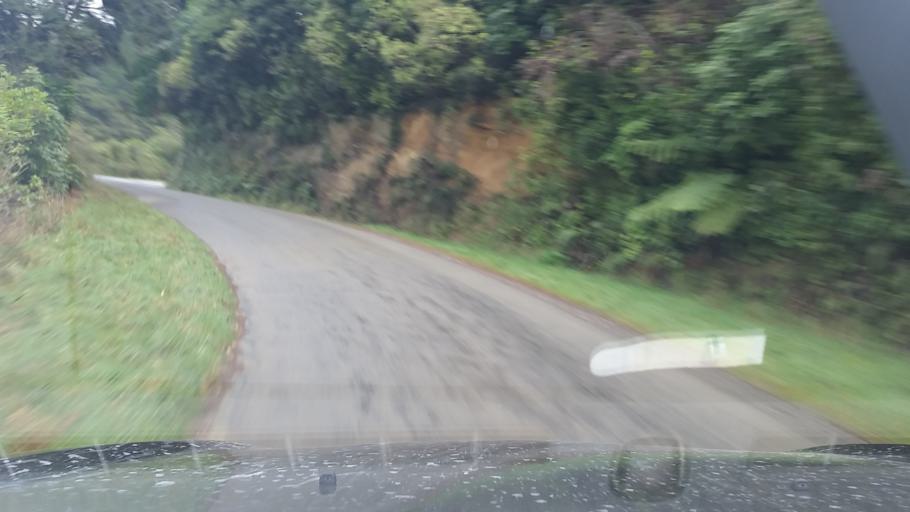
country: NZ
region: Marlborough
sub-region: Marlborough District
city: Picton
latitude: -41.1756
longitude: 174.0582
